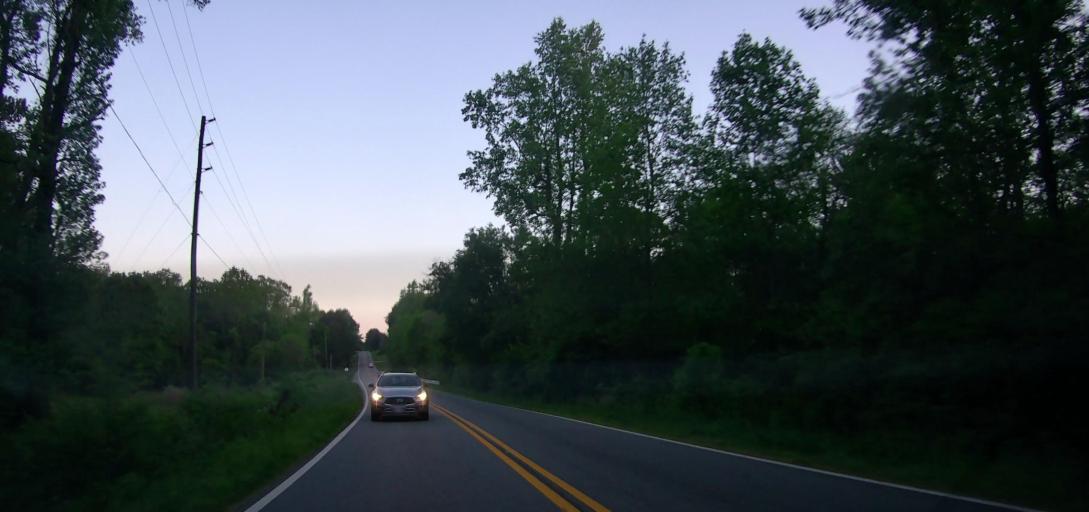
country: US
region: Georgia
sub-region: Henry County
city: McDonough
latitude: 33.4692
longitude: -84.1945
